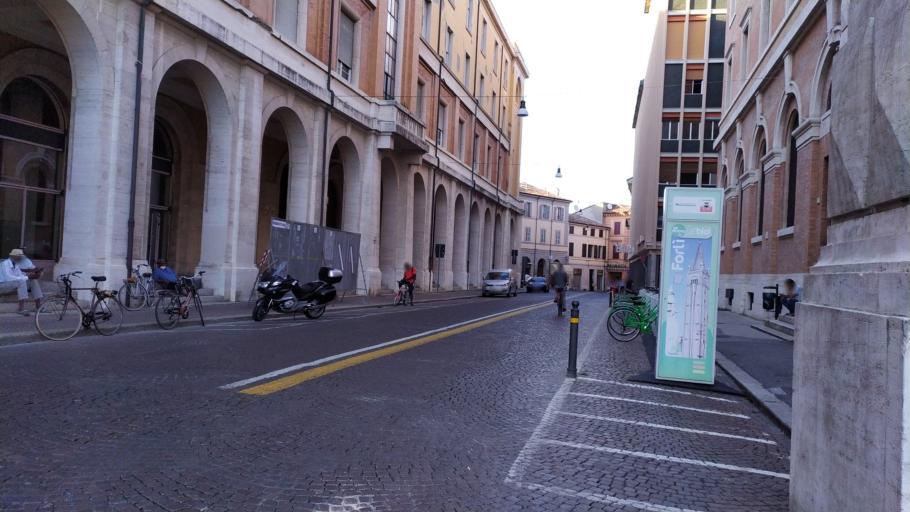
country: IT
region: Emilia-Romagna
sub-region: Forli-Cesena
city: Forli
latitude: 44.2233
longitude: 12.0414
